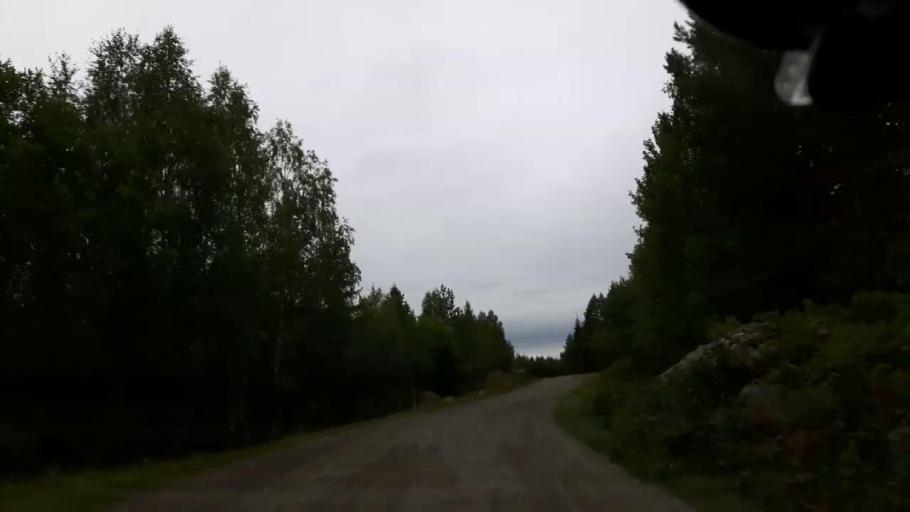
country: SE
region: Vaesternorrland
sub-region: Ange Kommun
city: Fransta
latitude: 62.8588
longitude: 15.9825
